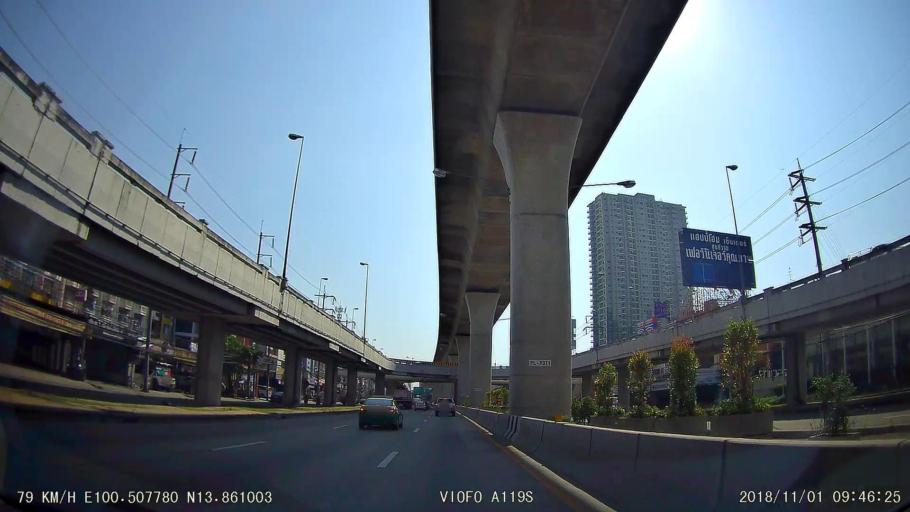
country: TH
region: Nonthaburi
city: Mueang Nonthaburi
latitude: 13.8610
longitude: 100.5079
